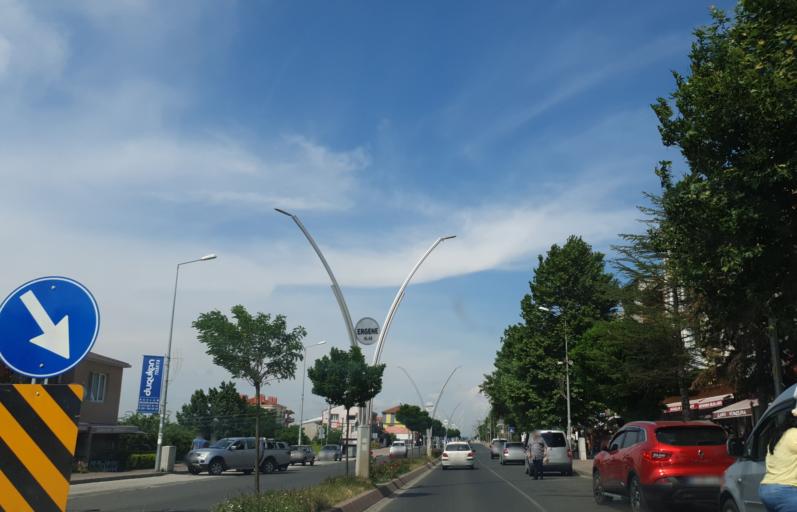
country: TR
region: Tekirdag
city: Marmaracik
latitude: 41.2357
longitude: 27.7079
